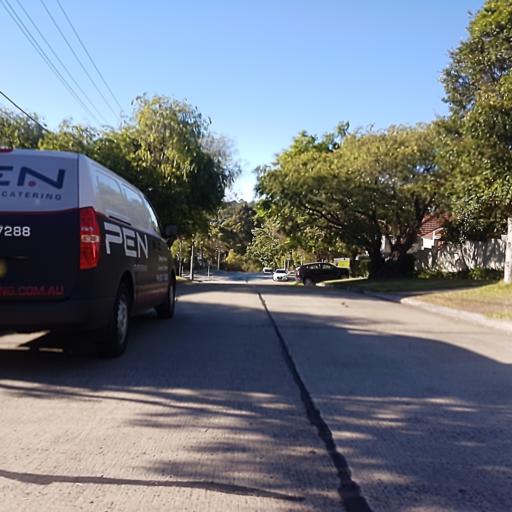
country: AU
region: New South Wales
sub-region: Willoughby
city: Castle Cove
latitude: -33.7909
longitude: 151.2033
